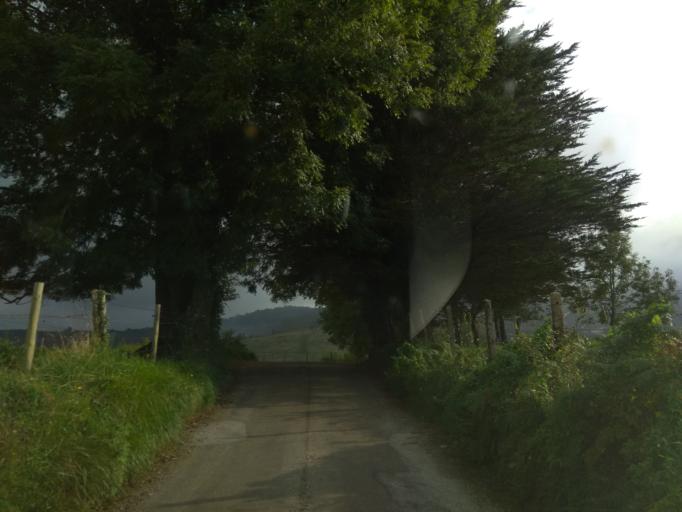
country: ES
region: Cantabria
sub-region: Provincia de Cantabria
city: San Vicente de la Barquera
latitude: 43.3109
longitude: -4.3908
